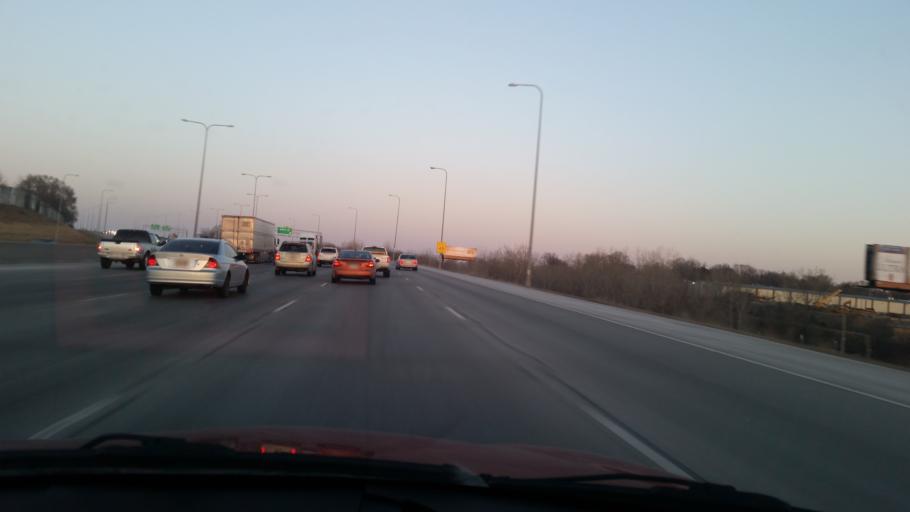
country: US
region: Nebraska
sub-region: Douglas County
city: Omaha
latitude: 41.2224
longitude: -95.9851
